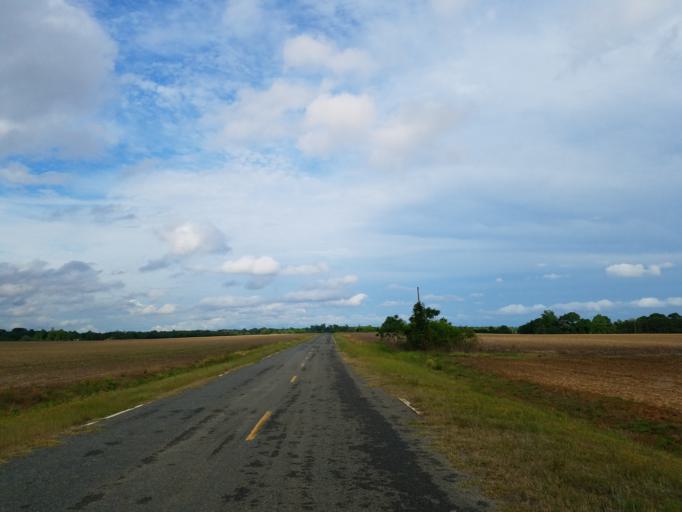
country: US
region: Georgia
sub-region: Dooly County
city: Unadilla
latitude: 32.2130
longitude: -83.7536
